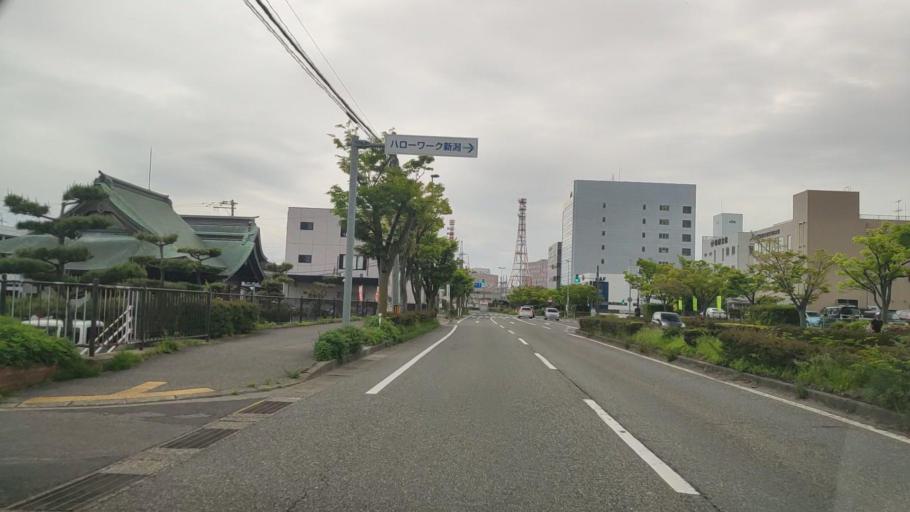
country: JP
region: Niigata
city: Niigata-shi
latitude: 37.9001
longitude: 139.0230
